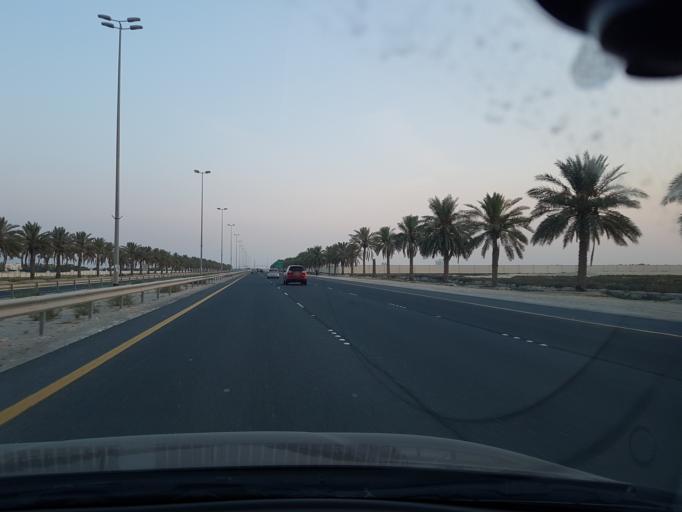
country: BH
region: Central Governorate
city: Dar Kulayb
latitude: 26.0448
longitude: 50.4998
